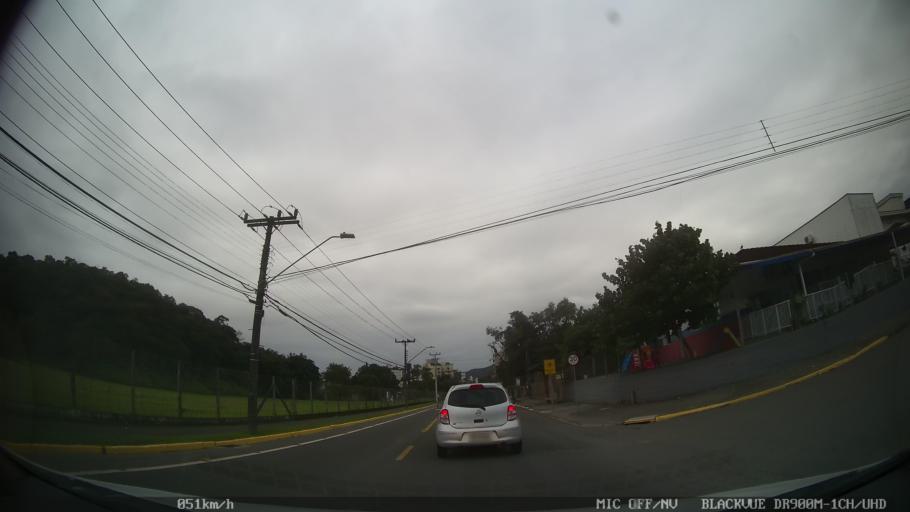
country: BR
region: Santa Catarina
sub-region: Joinville
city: Joinville
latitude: -26.2846
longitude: -48.8584
